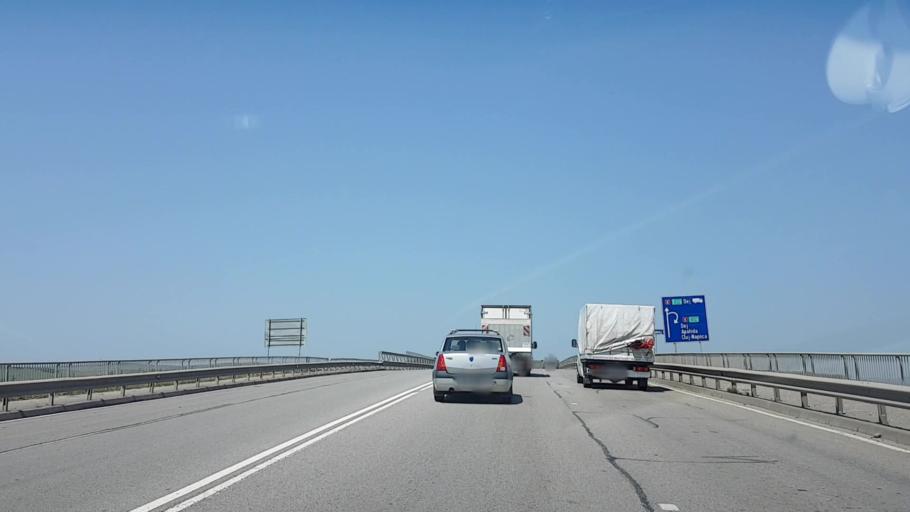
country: RO
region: Cluj
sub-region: Comuna Apahida
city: Sannicoara
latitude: 46.7803
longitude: 23.7034
